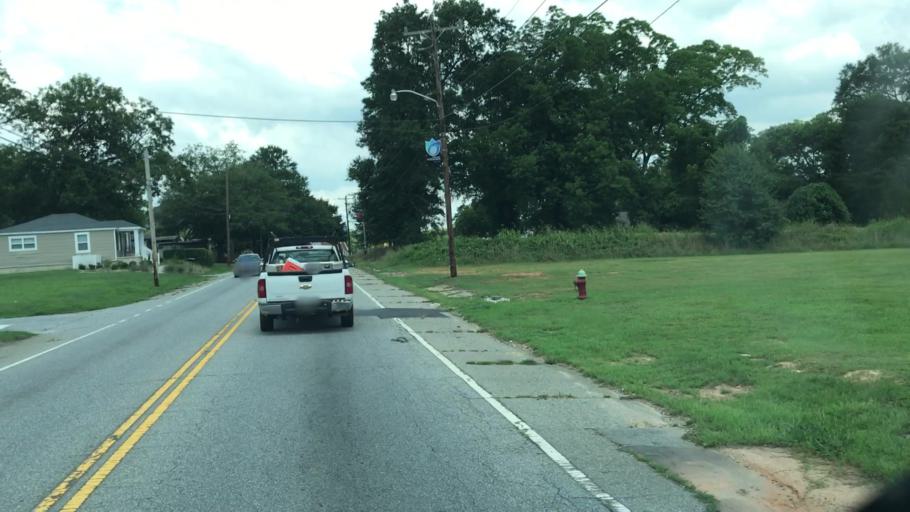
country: US
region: South Carolina
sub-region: Anderson County
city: Williamston
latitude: 34.6250
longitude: -82.4708
